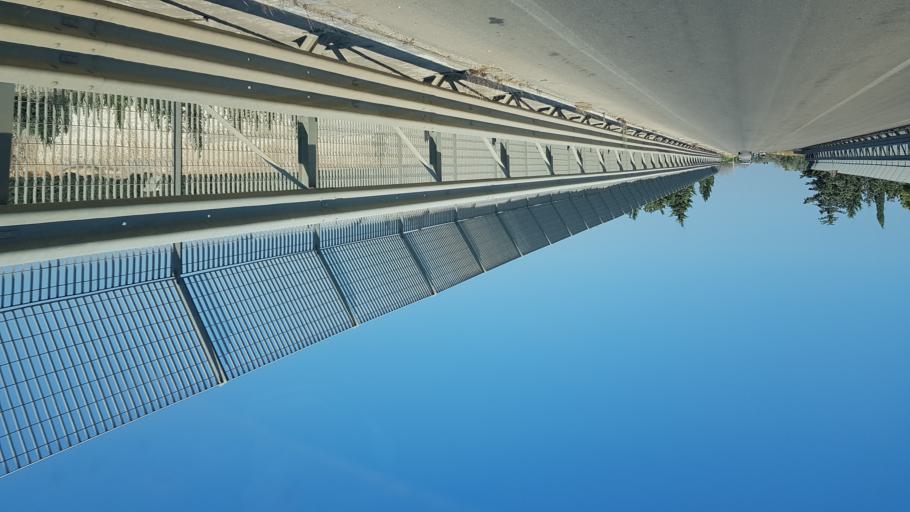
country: IT
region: Apulia
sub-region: Provincia di Lecce
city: Veglie
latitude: 40.3475
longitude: 17.9520
